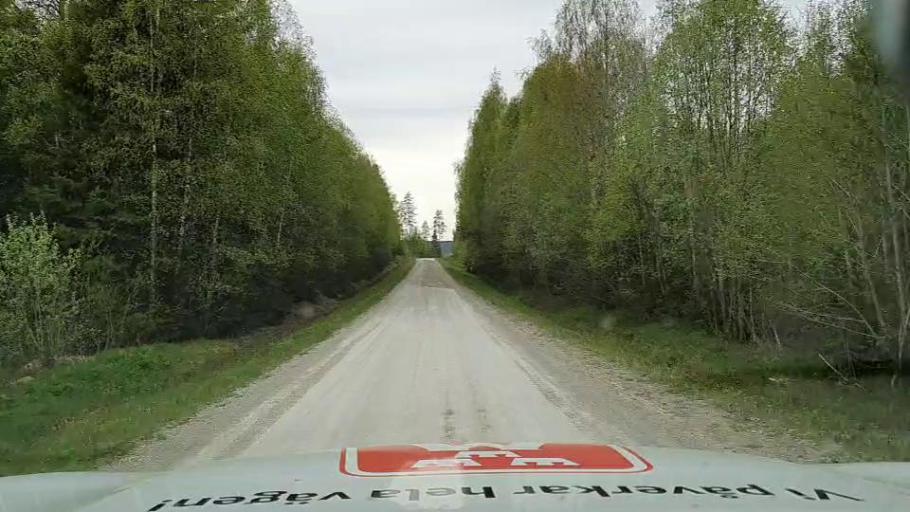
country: SE
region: Jaemtland
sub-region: Bergs Kommun
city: Hoverberg
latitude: 62.6774
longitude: 14.7608
